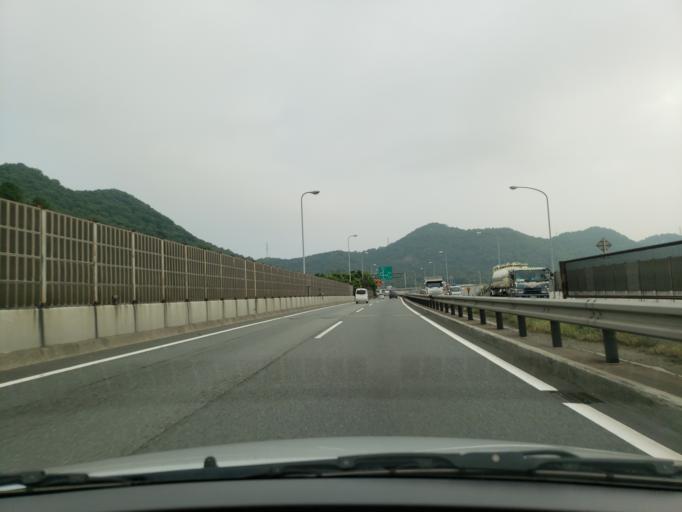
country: JP
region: Hyogo
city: Himeji
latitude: 34.8251
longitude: 134.6353
